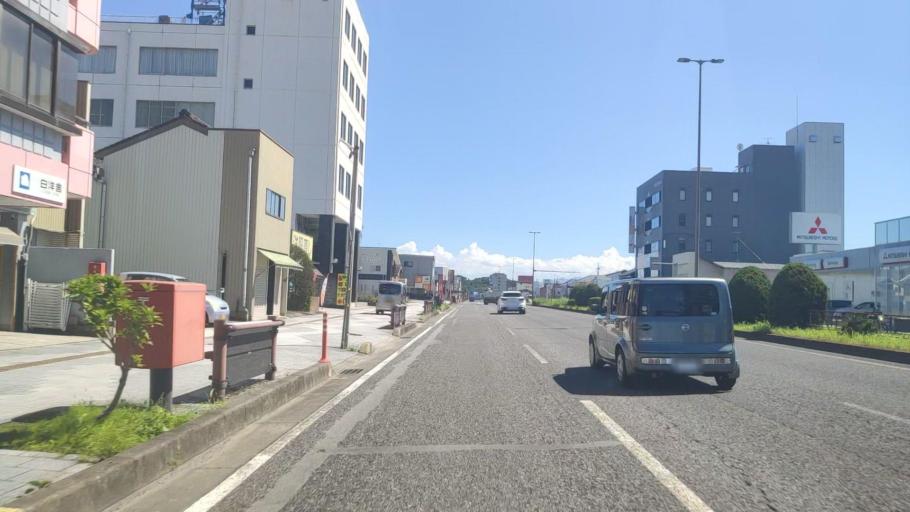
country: JP
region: Mie
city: Tsu-shi
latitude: 34.7118
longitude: 136.5086
